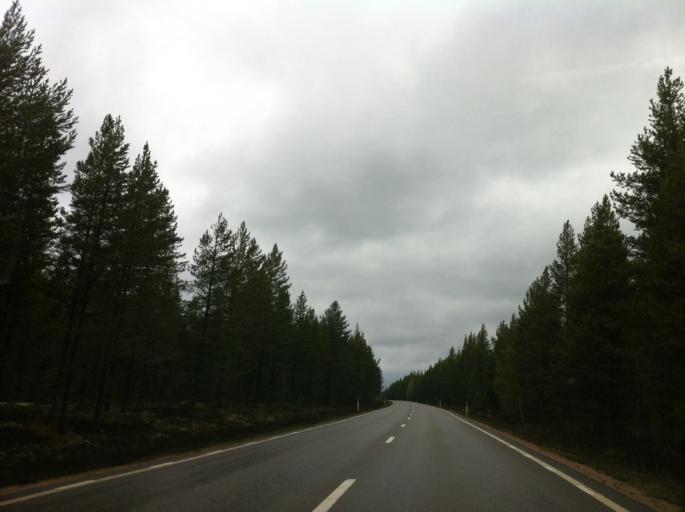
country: SE
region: Jaemtland
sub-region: Harjedalens Kommun
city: Sveg
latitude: 62.0573
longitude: 14.2973
